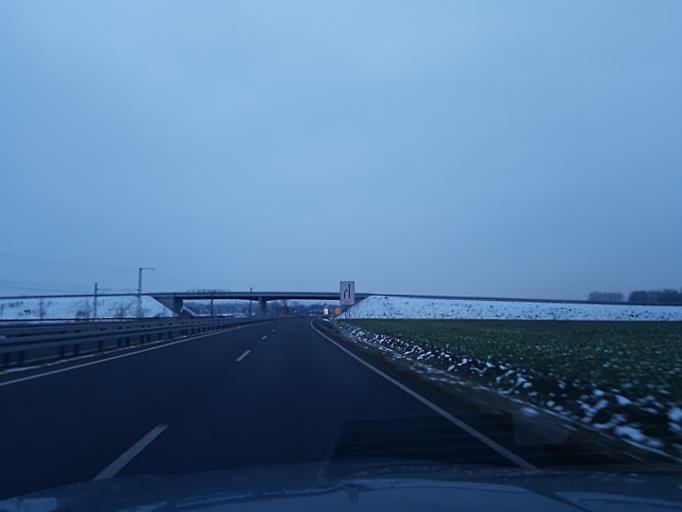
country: DE
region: Saxony
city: Stauchitz
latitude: 51.2766
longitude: 13.2495
